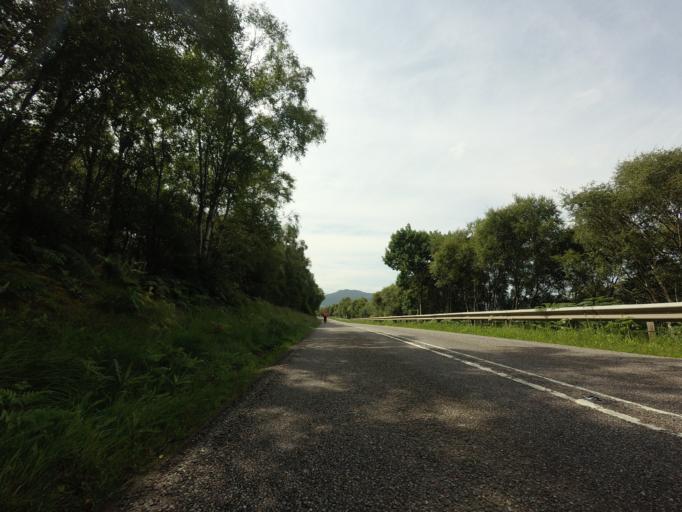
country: GB
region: Scotland
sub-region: Highland
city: Alness
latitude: 57.8558
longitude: -4.2526
